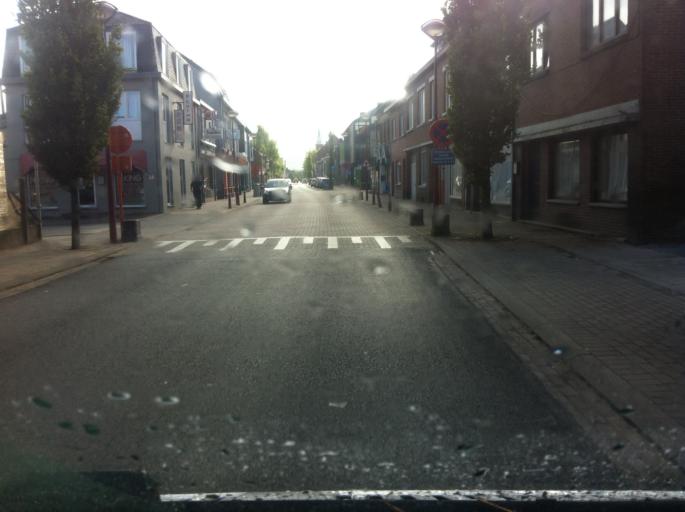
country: BE
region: Flanders
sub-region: Provincie Limburg
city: Maasmechelen
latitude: 50.9627
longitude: 5.6985
